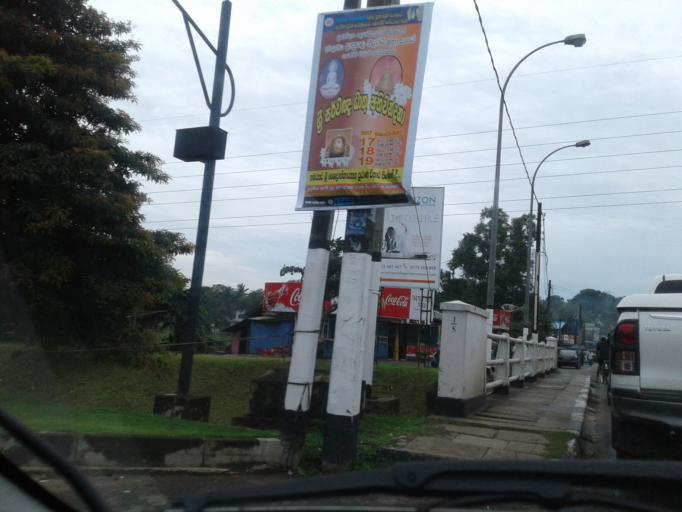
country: LK
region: Western
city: Mulleriyawa
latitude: 6.9057
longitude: 79.9632
